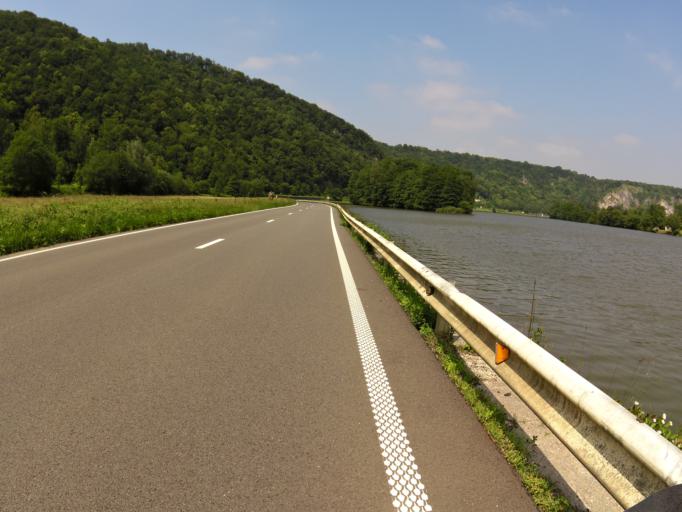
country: BE
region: Wallonia
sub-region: Province de Namur
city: Dinant
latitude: 50.2359
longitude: 4.8877
